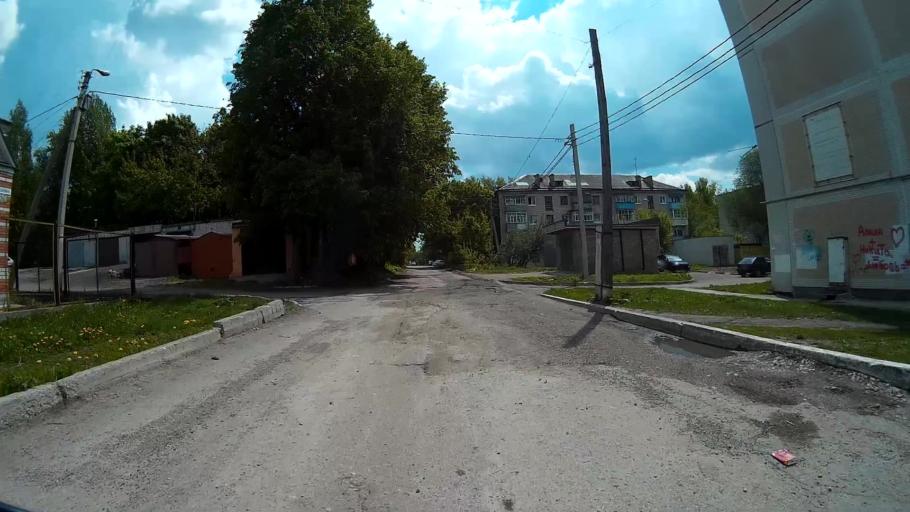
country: RU
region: Ulyanovsk
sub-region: Ulyanovskiy Rayon
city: Ulyanovsk
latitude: 54.3422
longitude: 48.3685
